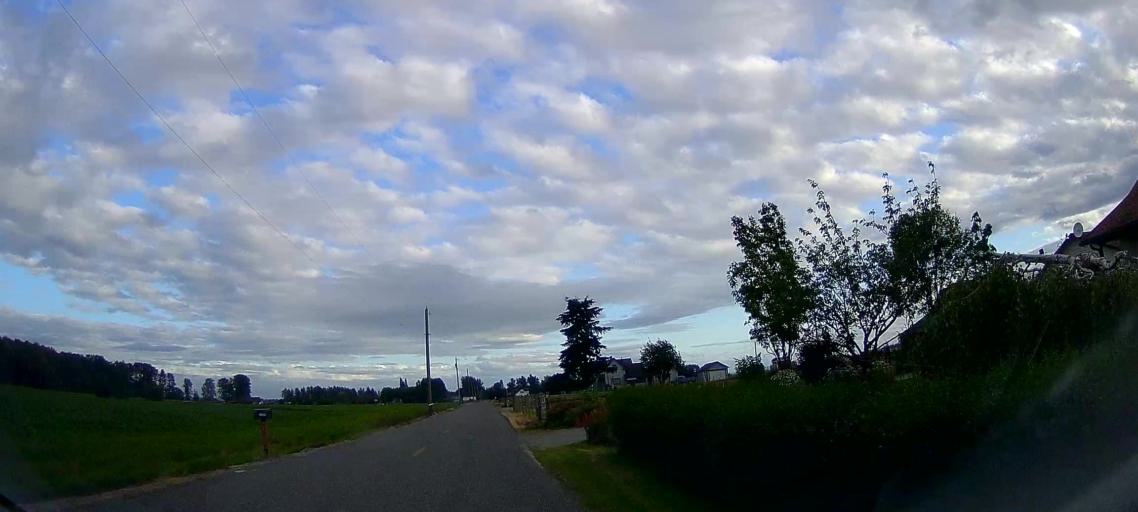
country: US
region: Washington
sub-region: Skagit County
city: Mount Vernon
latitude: 48.3952
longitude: -122.3844
